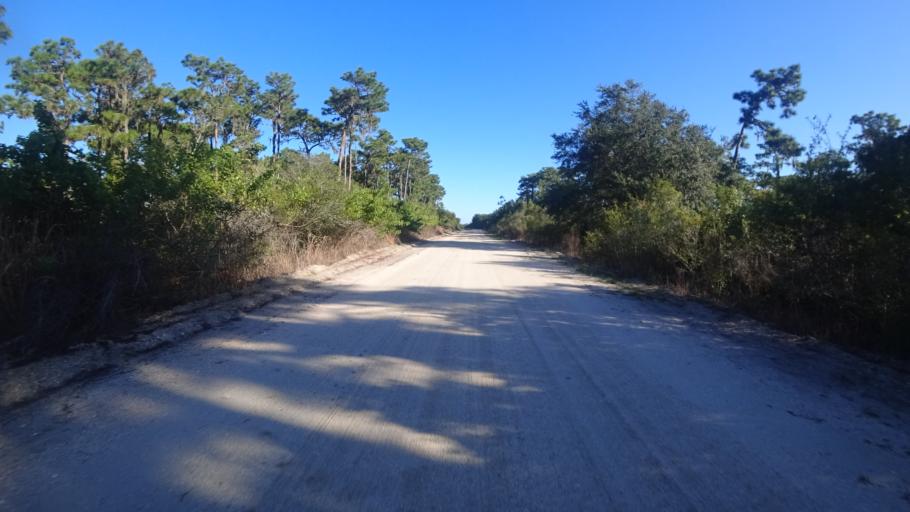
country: US
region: Florida
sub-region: Hillsborough County
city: Ruskin
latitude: 27.6323
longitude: -82.4391
